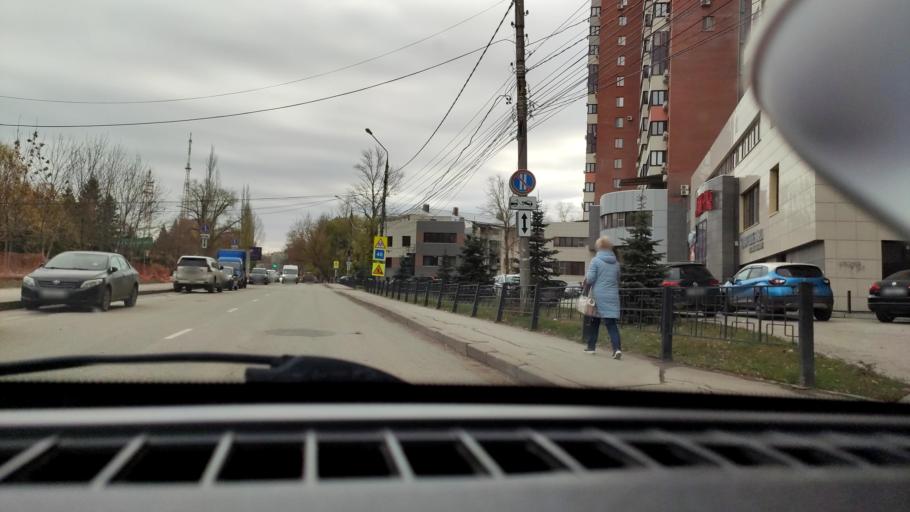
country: RU
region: Samara
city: Samara
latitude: 53.2379
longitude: 50.1815
